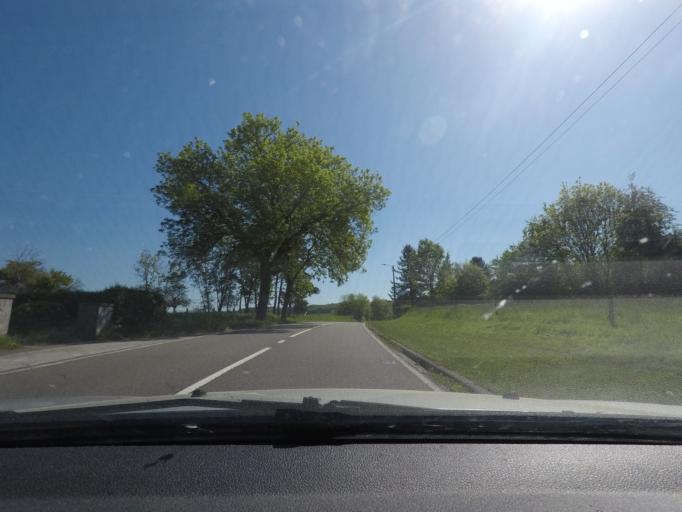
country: BE
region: Wallonia
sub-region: Province de Namur
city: Houyet
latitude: 50.1677
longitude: 5.0903
